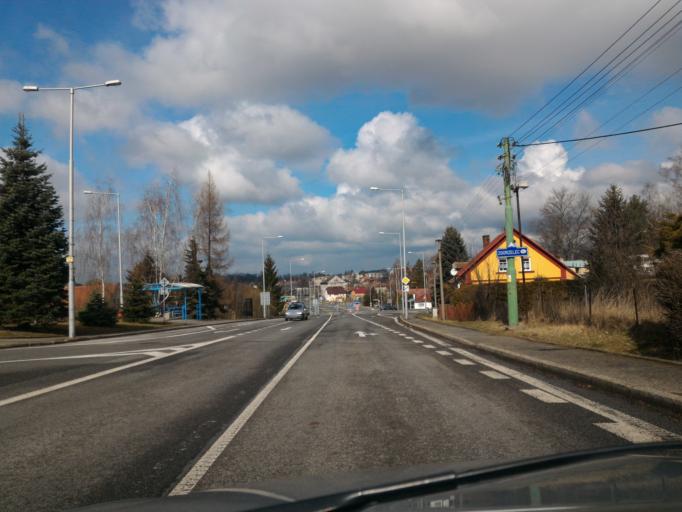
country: PL
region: Silesian Voivodeship
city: Zawidow
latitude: 51.0195
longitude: 15.0648
